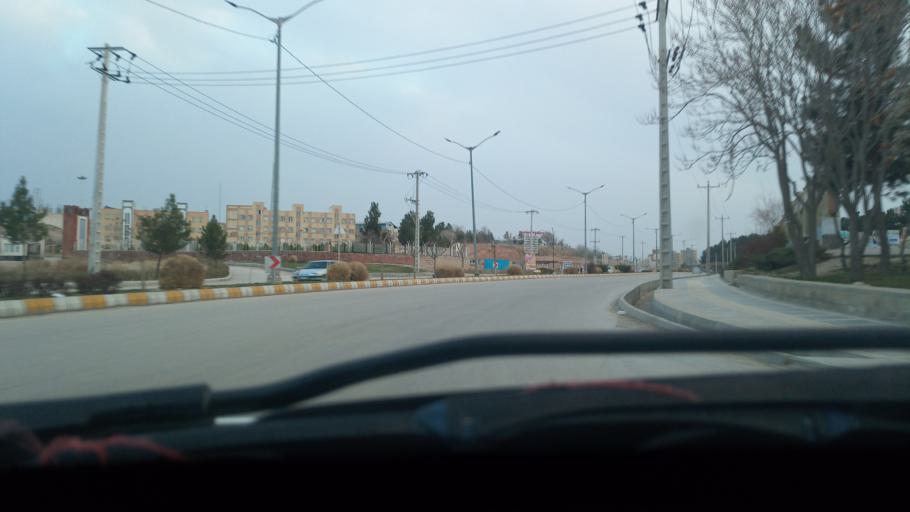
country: IR
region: Khorasan-e Shomali
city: Bojnurd
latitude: 37.4601
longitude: 57.3320
